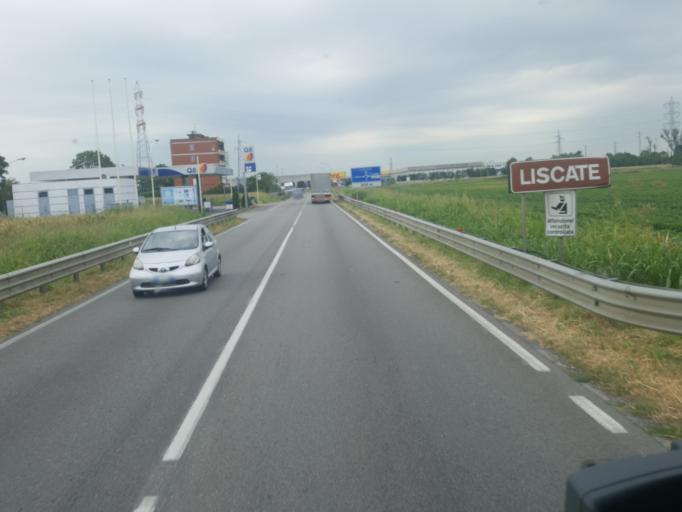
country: IT
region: Lombardy
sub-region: Citta metropolitana di Milano
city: Liscate
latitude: 45.4831
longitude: 9.4260
